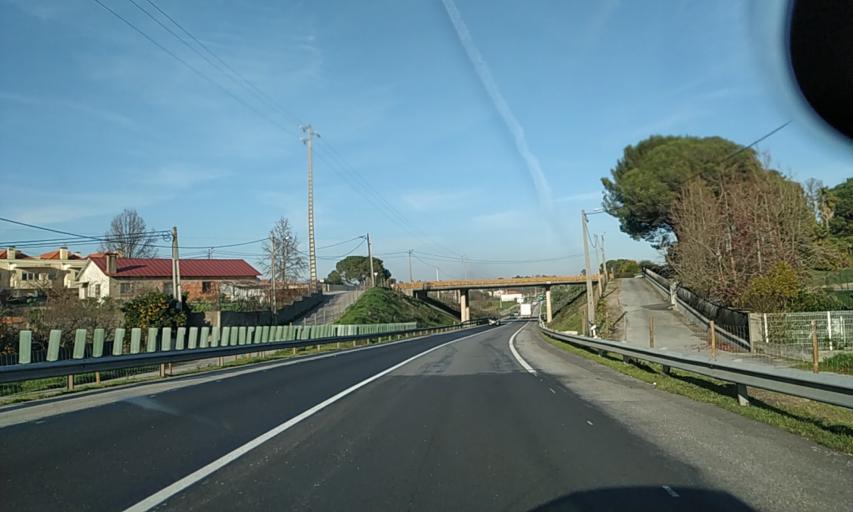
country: PT
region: Viseu
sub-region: Concelho de Tondela
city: Tondela
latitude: 40.5199
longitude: -8.0934
